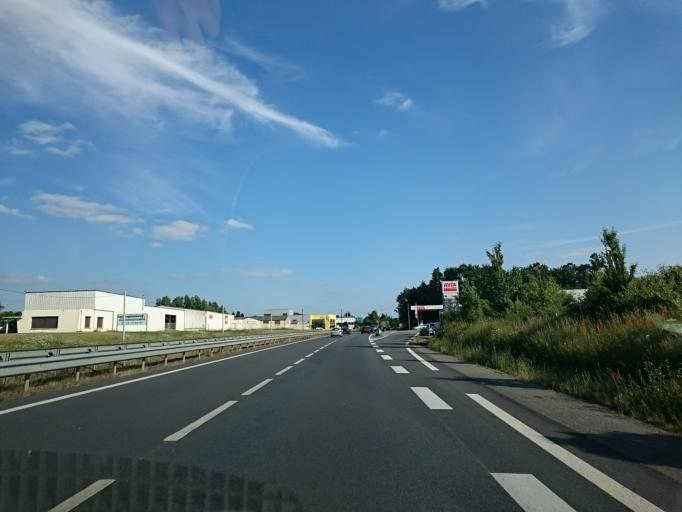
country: FR
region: Brittany
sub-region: Departement d'Ille-et-Vilaine
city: Vern-sur-Seiche
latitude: 48.0536
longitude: -1.6103
